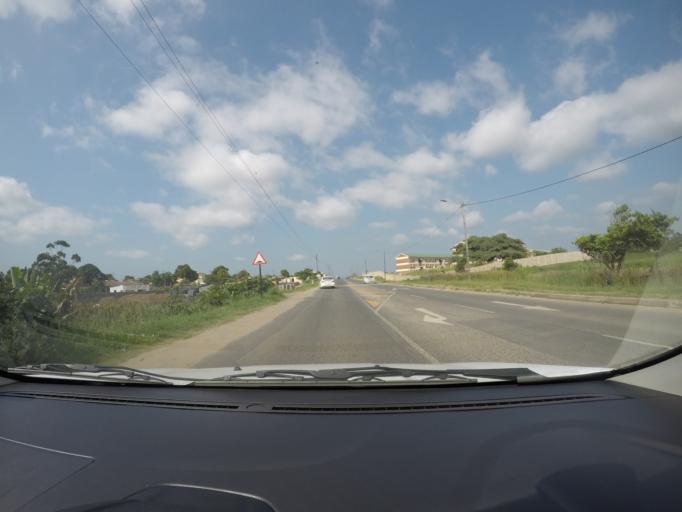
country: ZA
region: KwaZulu-Natal
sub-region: uThungulu District Municipality
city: eSikhawini
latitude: -28.8819
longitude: 31.9057
